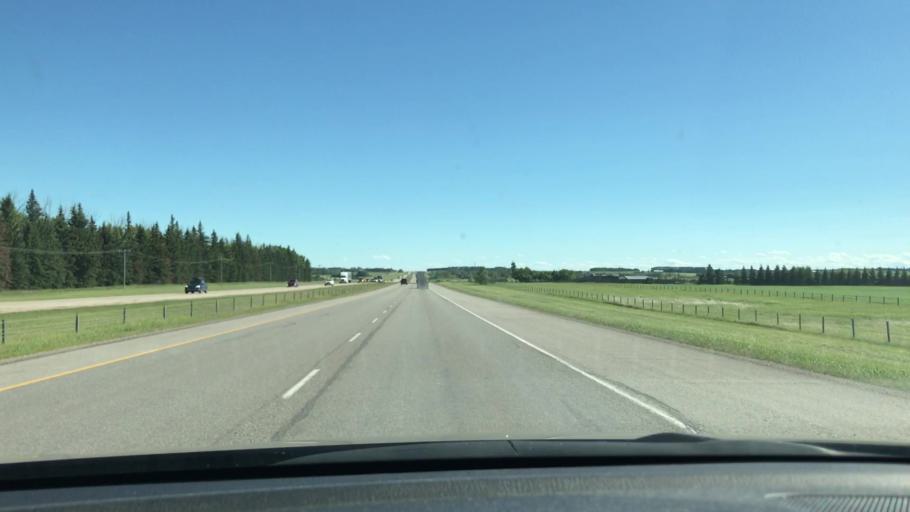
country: CA
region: Alberta
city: Olds
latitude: 51.9183
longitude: -114.0256
